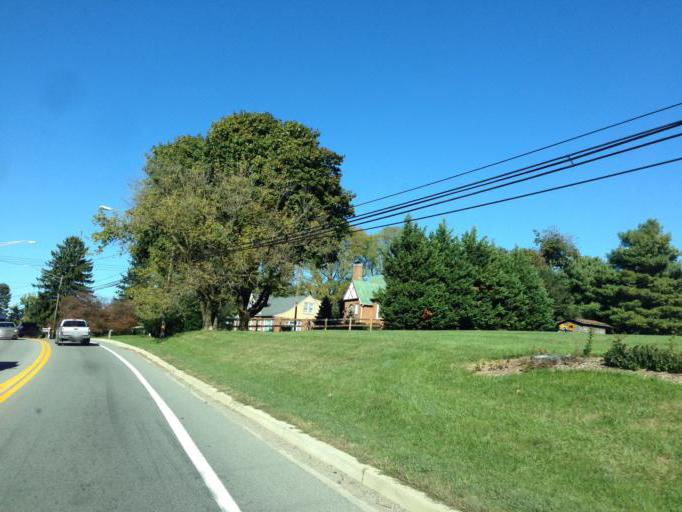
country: US
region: Maryland
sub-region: Montgomery County
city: Damascus
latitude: 39.3018
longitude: -77.1975
